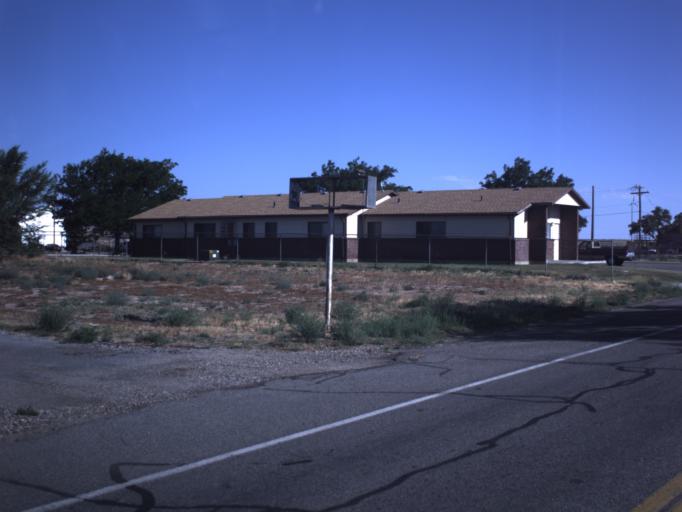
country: US
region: Utah
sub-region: Beaver County
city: Milford
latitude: 38.4021
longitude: -113.0098
